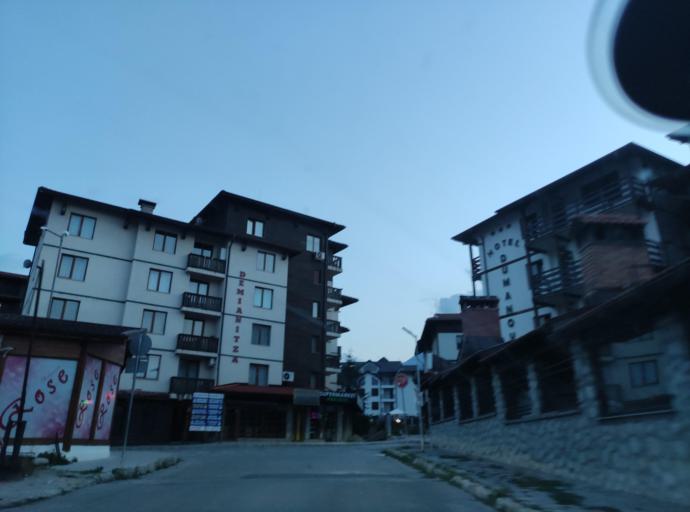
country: BG
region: Blagoevgrad
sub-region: Obshtina Bansko
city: Bansko
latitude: 41.8275
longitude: 23.4825
